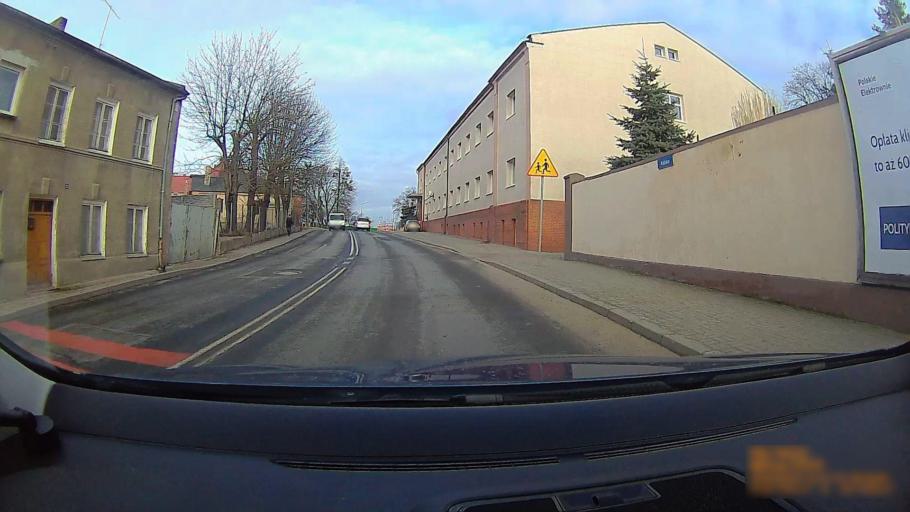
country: PL
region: Greater Poland Voivodeship
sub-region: Konin
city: Konin
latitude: 52.2025
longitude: 18.2483
